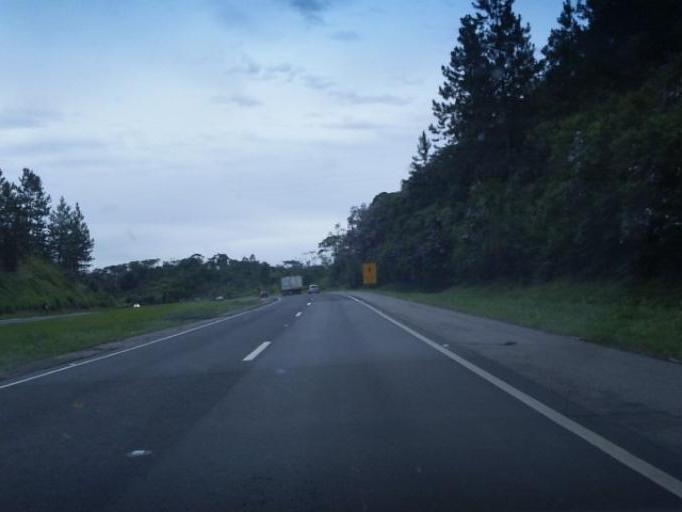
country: BR
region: Sao Paulo
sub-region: Juquia
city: Juquia
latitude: -24.3988
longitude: -47.7332
